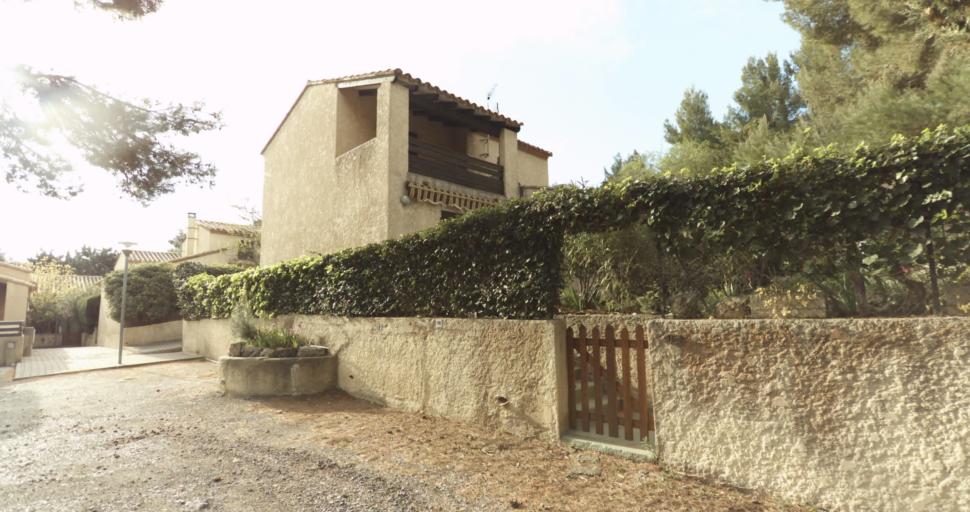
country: FR
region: Languedoc-Roussillon
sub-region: Departement de l'Aude
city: Leucate
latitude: 42.9341
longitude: 3.0284
